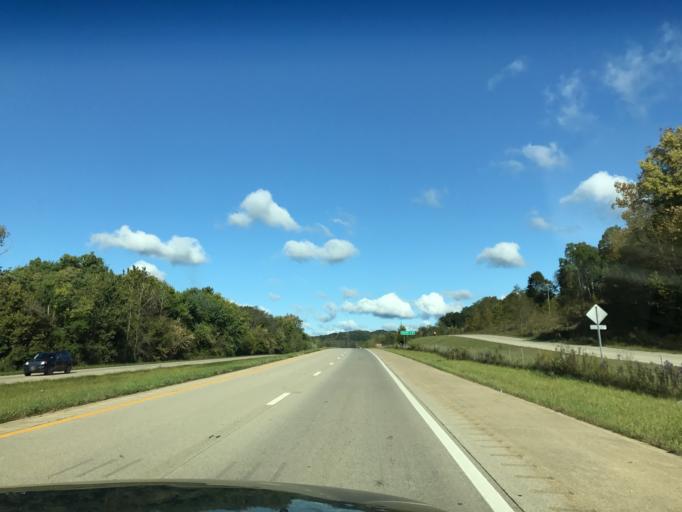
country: US
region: Ohio
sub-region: Athens County
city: Athens
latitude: 39.3205
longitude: -81.9903
